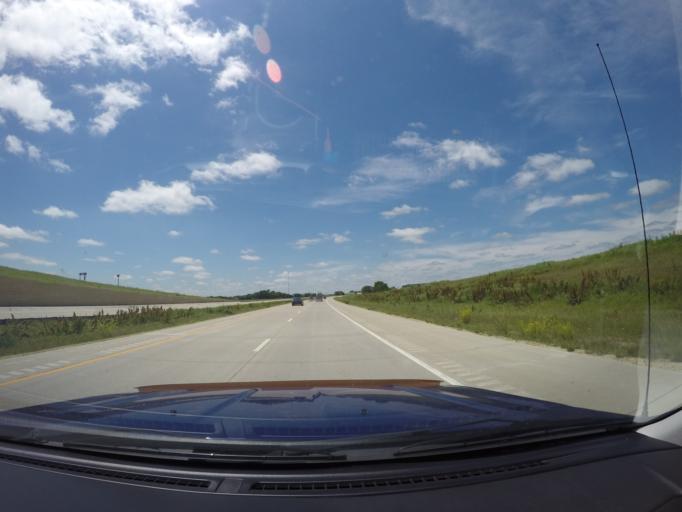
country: US
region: Kansas
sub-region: Riley County
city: Ogden
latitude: 39.1295
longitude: -96.6740
